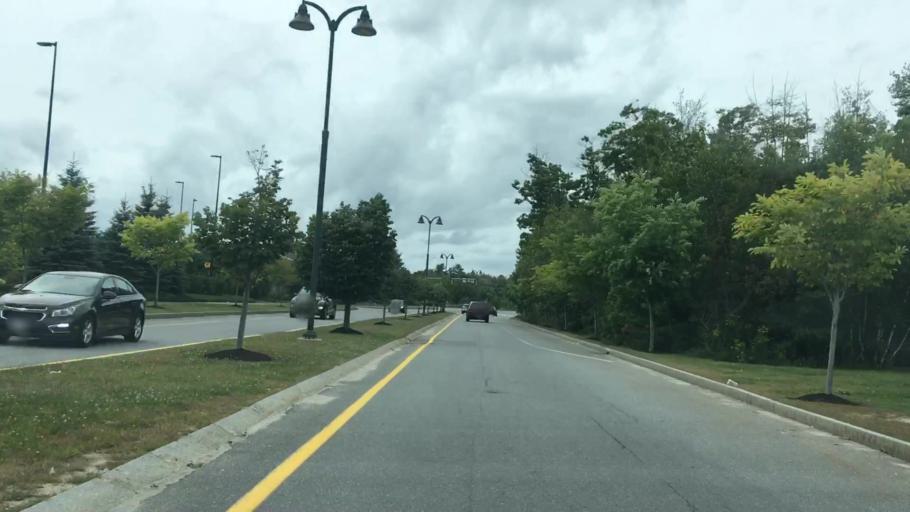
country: US
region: Maine
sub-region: Cumberland County
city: South Portland Gardens
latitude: 43.6244
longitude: -70.3440
